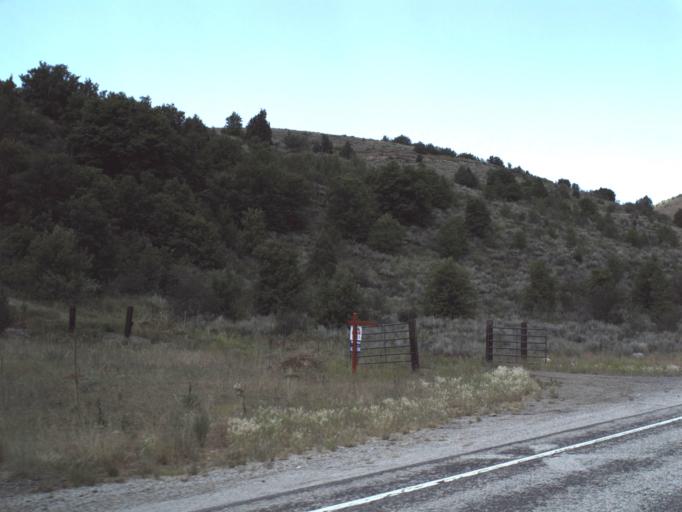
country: US
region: Utah
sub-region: Weber County
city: Wolf Creek
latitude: 41.3357
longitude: -111.6071
